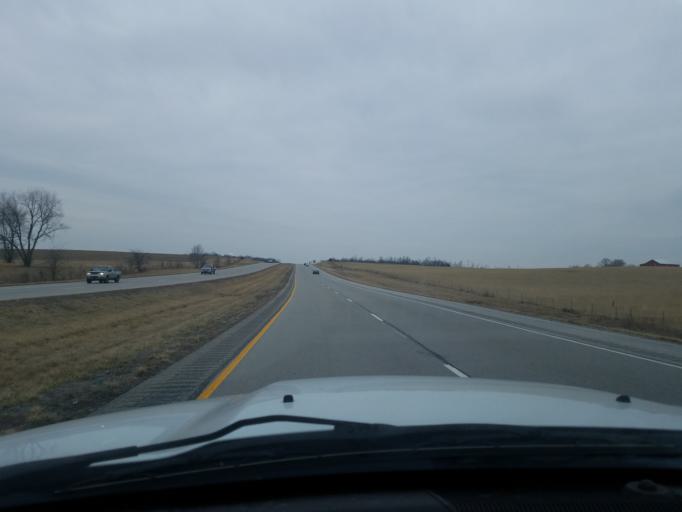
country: US
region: Kentucky
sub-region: Logan County
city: Auburn
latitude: 36.8901
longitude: -86.6555
